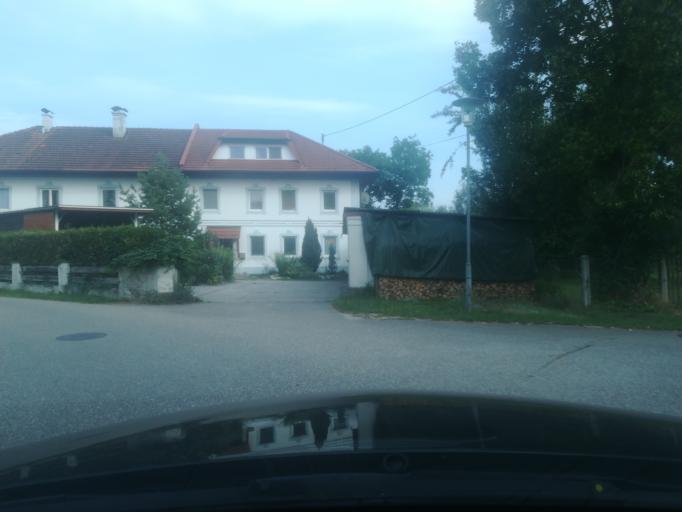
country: AT
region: Upper Austria
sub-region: Wels-Land
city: Marchtrenk
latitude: 48.1874
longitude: 14.1302
